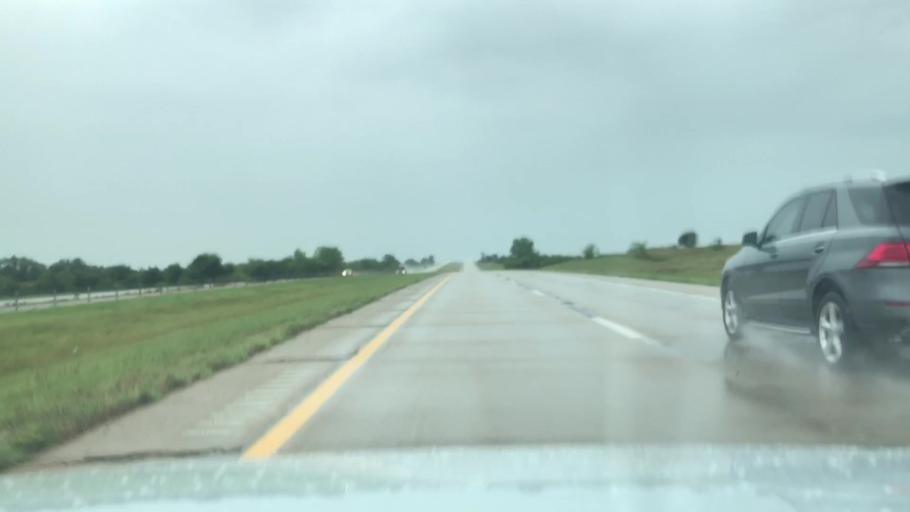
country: US
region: Oklahoma
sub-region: Osage County
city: Skiatook
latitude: 36.4068
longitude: -95.9204
